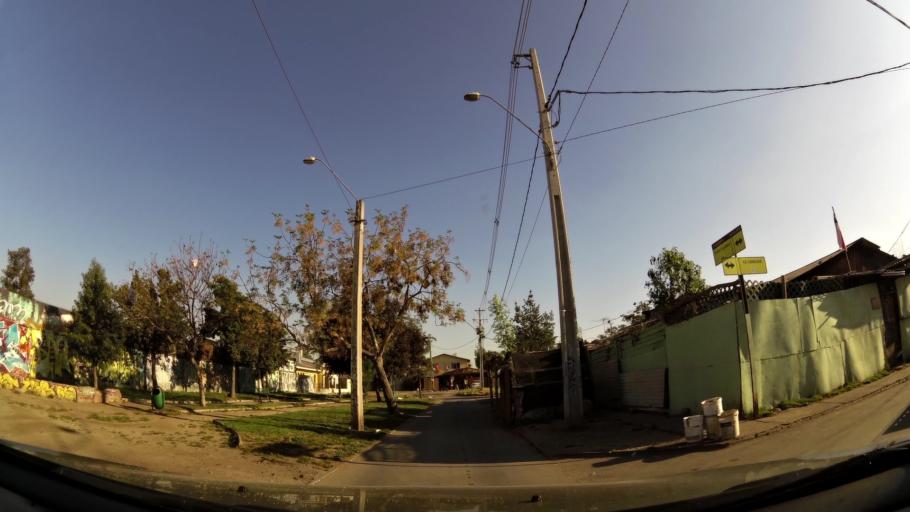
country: CL
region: Santiago Metropolitan
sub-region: Provincia de Santiago
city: La Pintana
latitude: -33.5783
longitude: -70.6581
